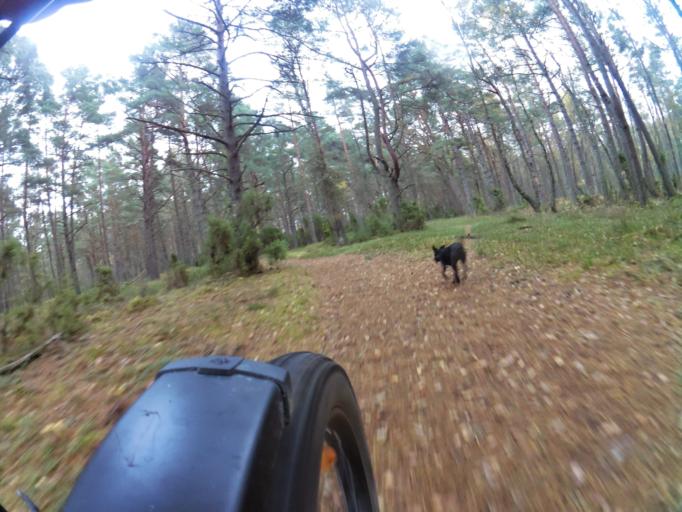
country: PL
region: Pomeranian Voivodeship
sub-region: Powiat leborski
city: Leba
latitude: 54.7752
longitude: 17.6780
